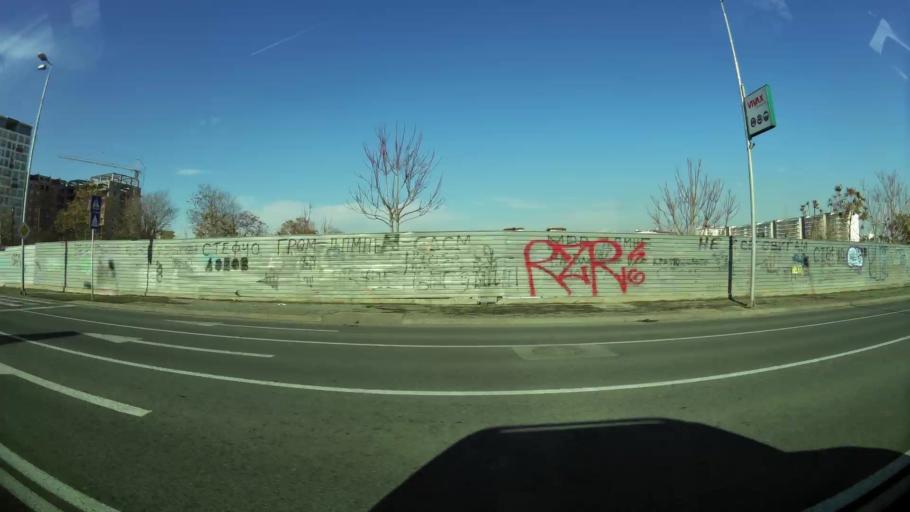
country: MK
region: Karpos
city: Skopje
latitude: 41.9970
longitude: 21.3999
